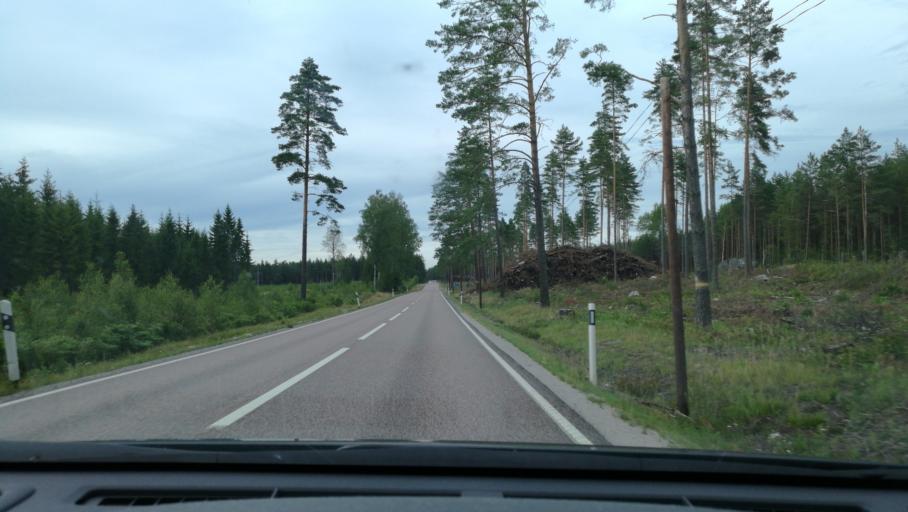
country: SE
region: Vaestmanland
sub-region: Kungsors Kommun
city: Kungsoer
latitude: 59.3108
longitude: 16.1075
